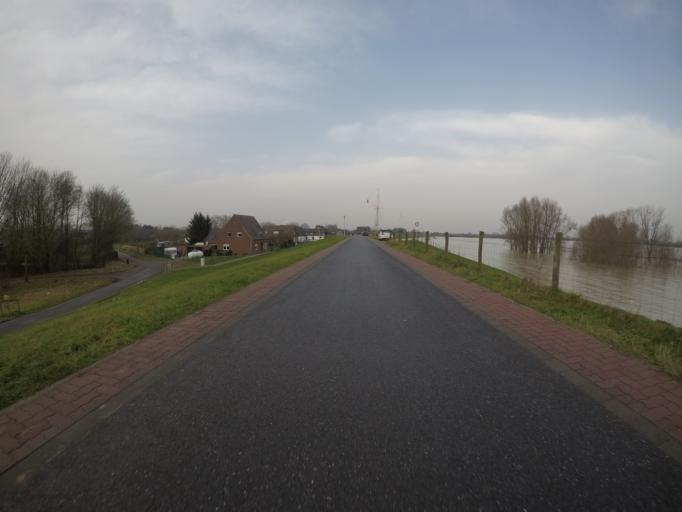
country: DE
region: North Rhine-Westphalia
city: Rees
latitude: 51.7129
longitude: 6.4089
